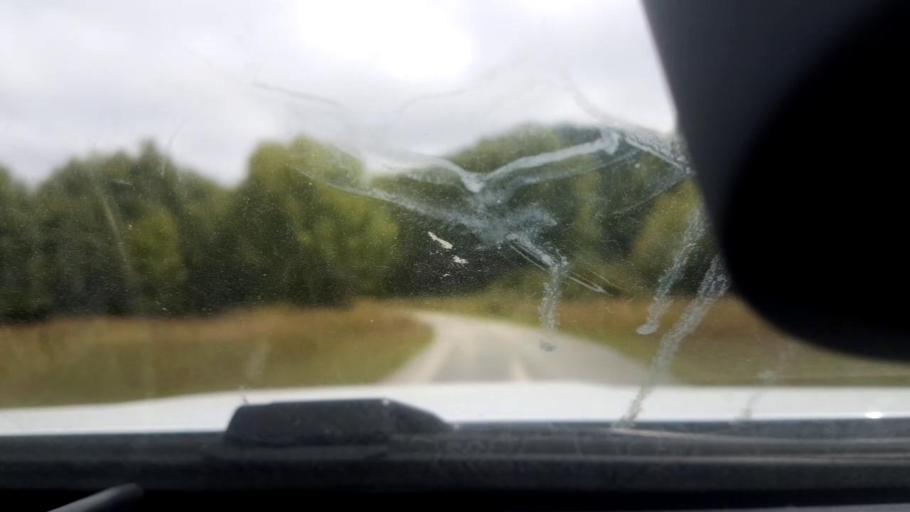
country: NZ
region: Canterbury
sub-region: Timaru District
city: Pleasant Point
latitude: -44.1426
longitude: 171.0861
